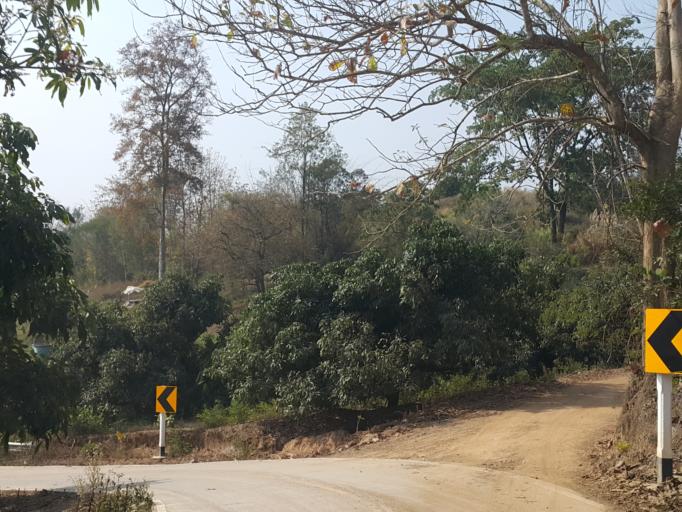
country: TH
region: Chiang Mai
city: Hang Dong
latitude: 18.7371
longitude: 98.8608
